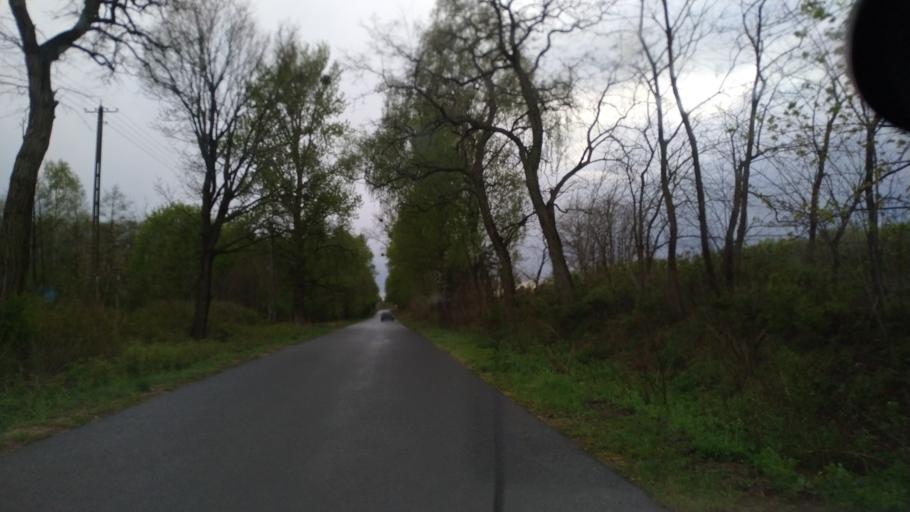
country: PL
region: Pomeranian Voivodeship
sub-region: Powiat starogardzki
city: Osiek
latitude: 53.6425
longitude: 18.4857
